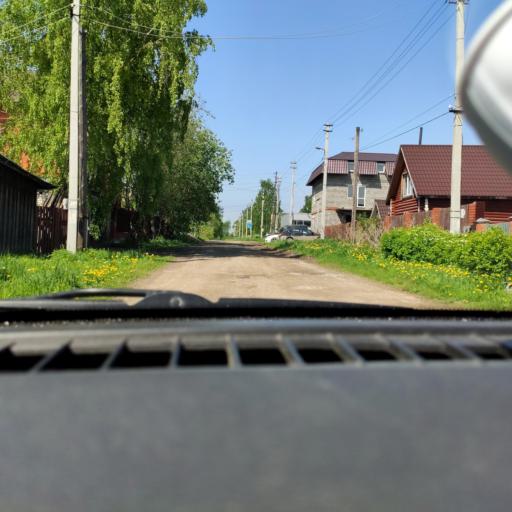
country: RU
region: Perm
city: Perm
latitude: 58.0447
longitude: 56.3303
